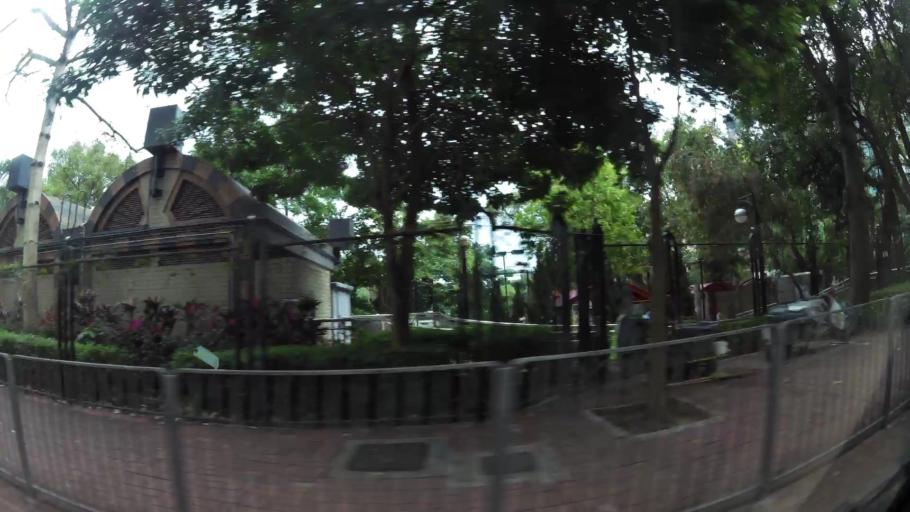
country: HK
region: Kowloon City
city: Kowloon
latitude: 22.3041
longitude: 114.1735
